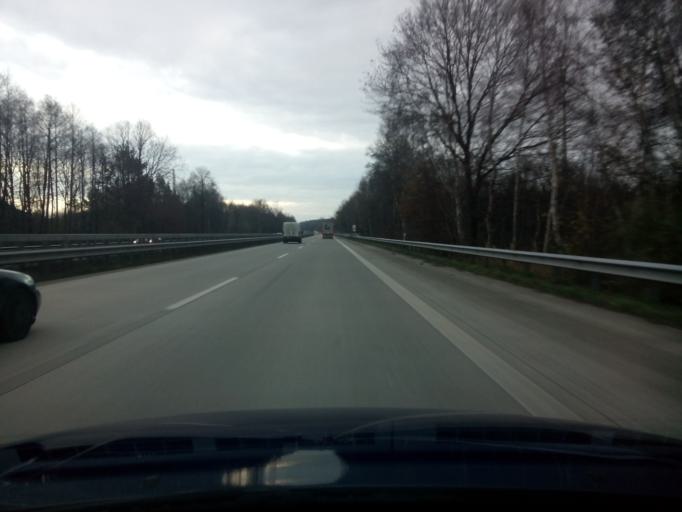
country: DE
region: Lower Saxony
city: Schwanewede
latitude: 53.2615
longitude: 8.6357
